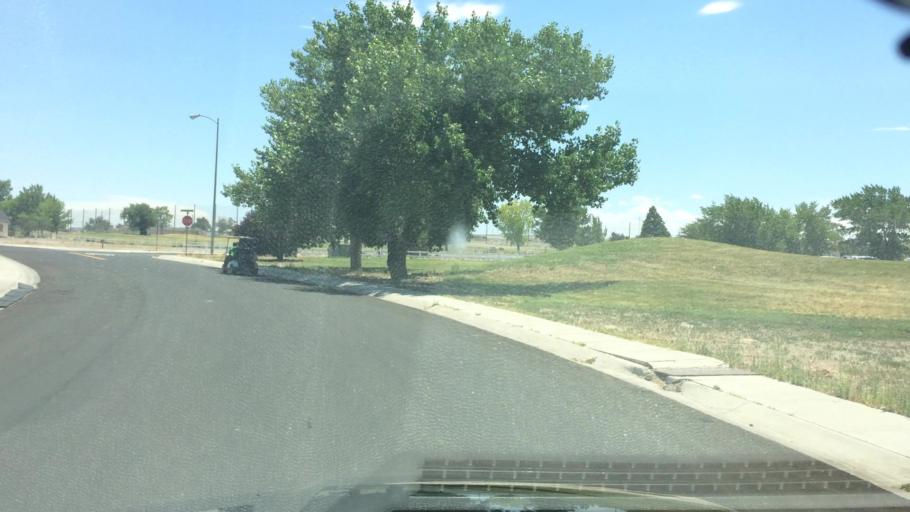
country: US
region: Nevada
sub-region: Lyon County
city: Fernley
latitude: 39.5848
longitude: -119.1511
